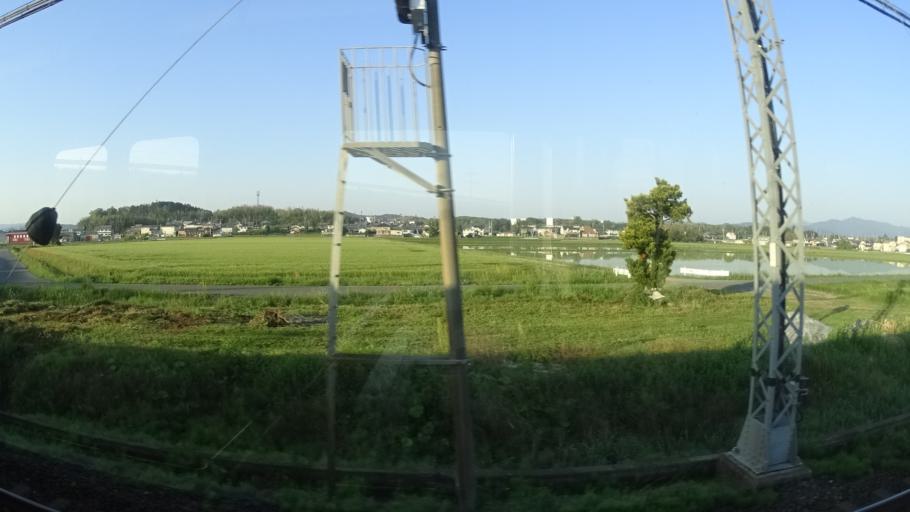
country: JP
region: Mie
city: Ise
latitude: 34.5523
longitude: 136.5749
